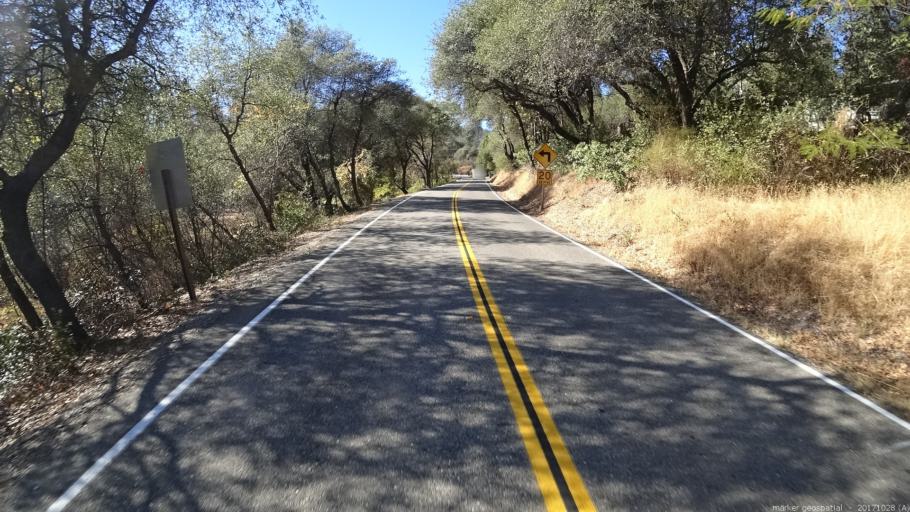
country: US
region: California
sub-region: Shasta County
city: Shasta
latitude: 40.6090
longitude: -122.4977
